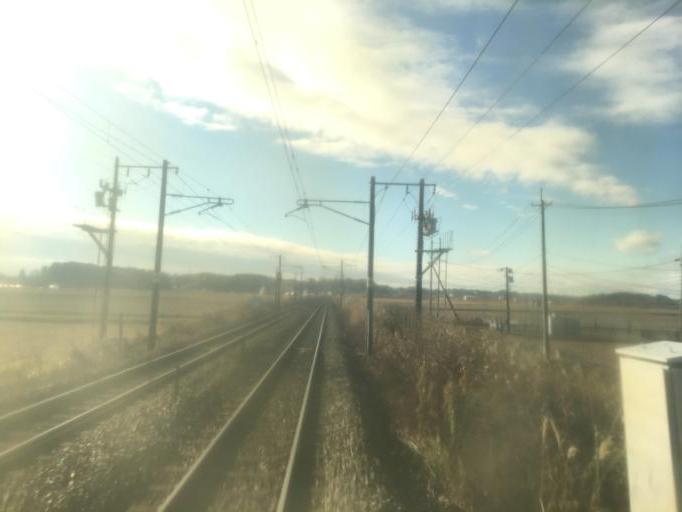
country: JP
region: Miyagi
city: Wakuya
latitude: 38.7283
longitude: 141.1354
